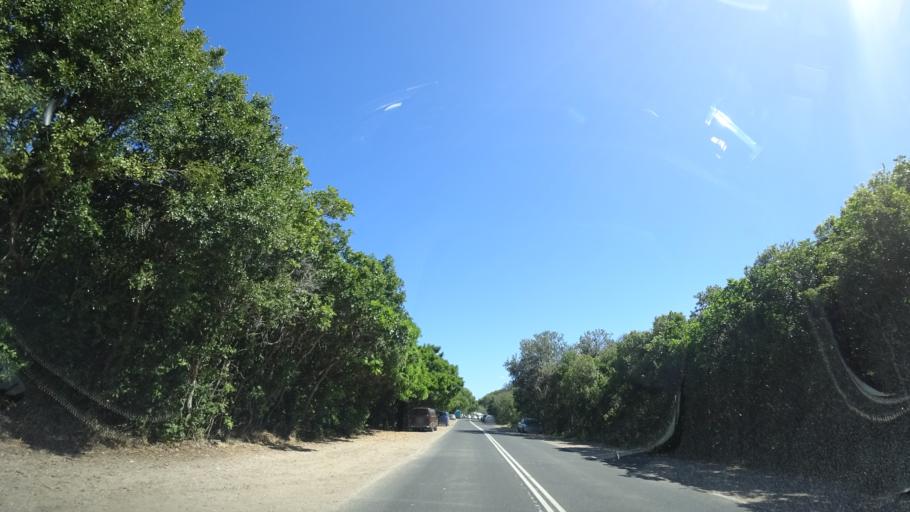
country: AU
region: Queensland
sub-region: Sunshine Coast
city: Mooloolaba
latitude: -26.6368
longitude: 153.1015
